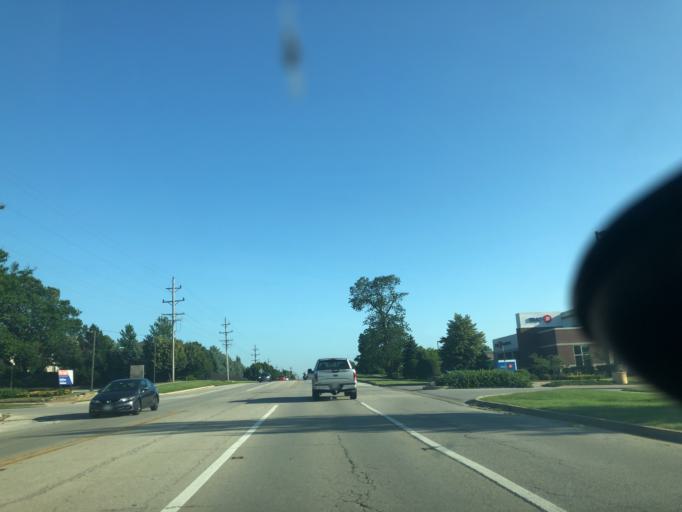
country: US
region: Illinois
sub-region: Will County
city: Mokena
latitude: 41.5629
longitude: -87.8904
